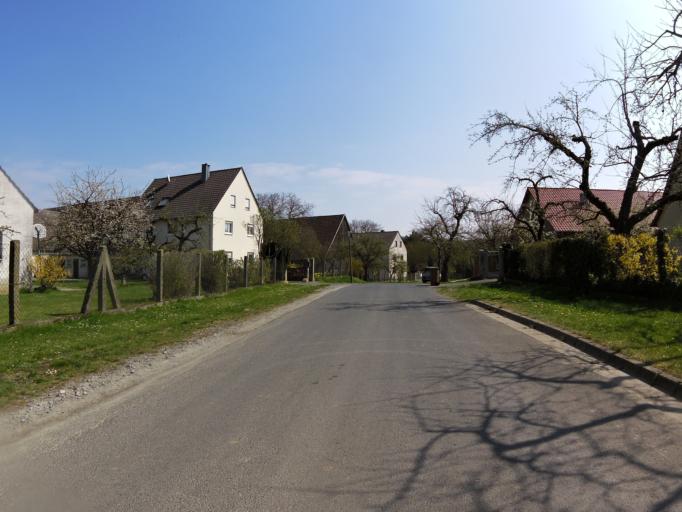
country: DE
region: Bavaria
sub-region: Regierungsbezirk Unterfranken
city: Rottendorf
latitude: 49.8123
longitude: 10.0557
